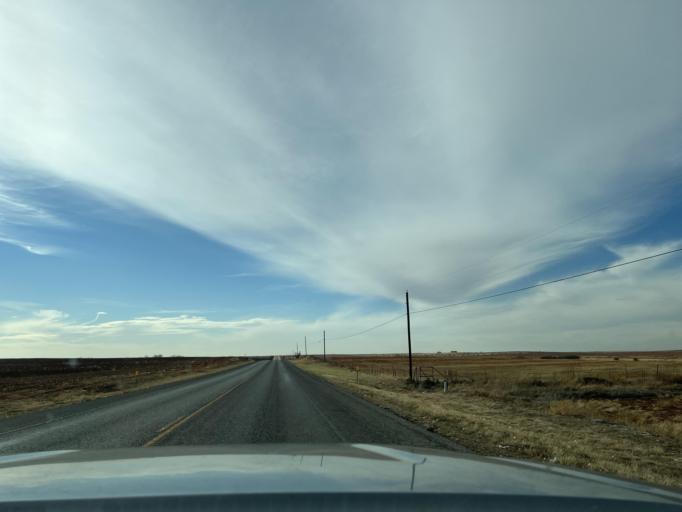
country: US
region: Texas
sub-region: Fisher County
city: Roby
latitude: 32.7413
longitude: -100.4643
